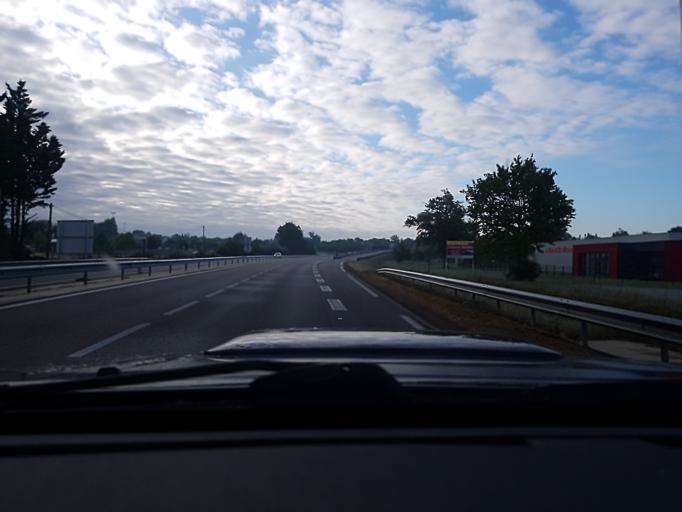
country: FR
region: Pays de la Loire
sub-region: Departement de la Vendee
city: Aizenay
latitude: 46.7494
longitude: -1.6265
